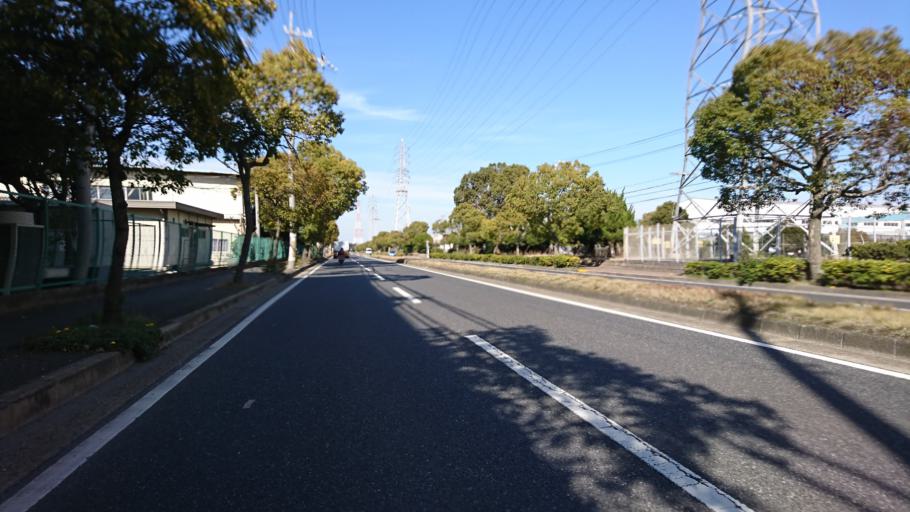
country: JP
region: Hyogo
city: Kakogawacho-honmachi
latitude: 34.7033
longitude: 134.8542
